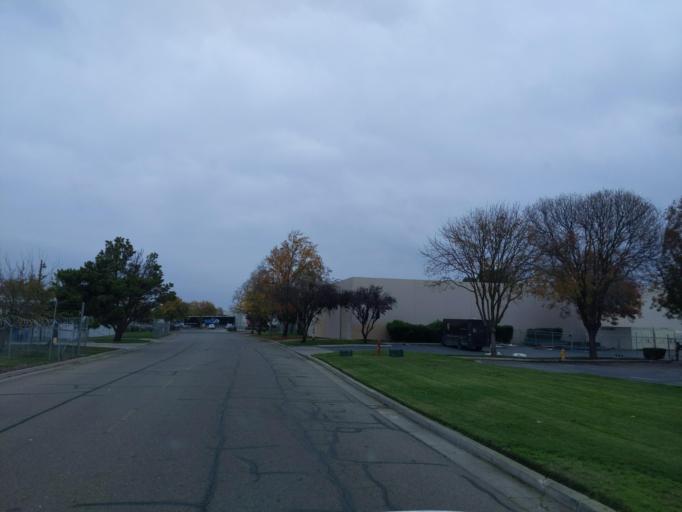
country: US
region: California
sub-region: San Joaquin County
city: Kennedy
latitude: 37.9366
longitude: -121.2313
